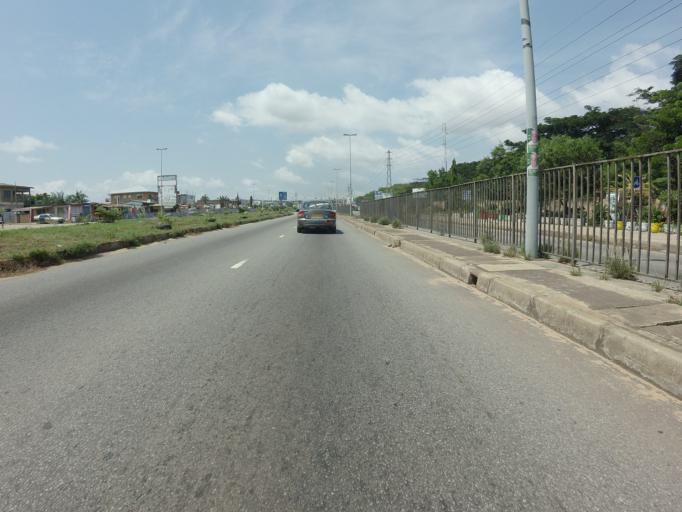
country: GH
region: Greater Accra
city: Gbawe
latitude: 5.5908
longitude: -0.2854
